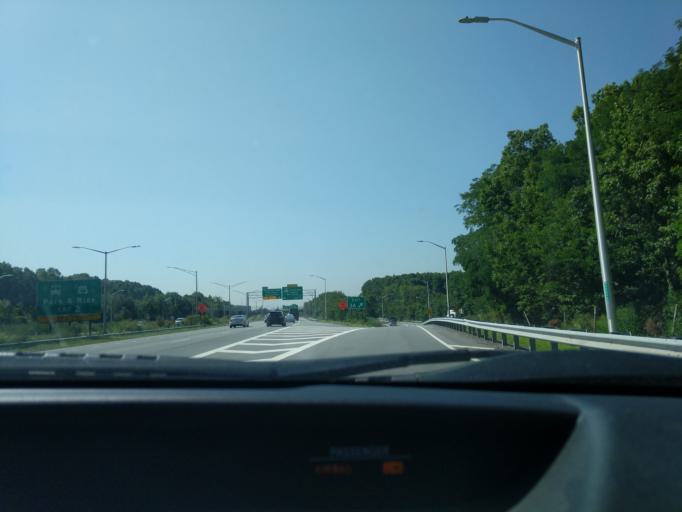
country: US
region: New Jersey
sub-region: Middlesex County
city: Sewaren
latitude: 40.5365
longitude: -74.2246
